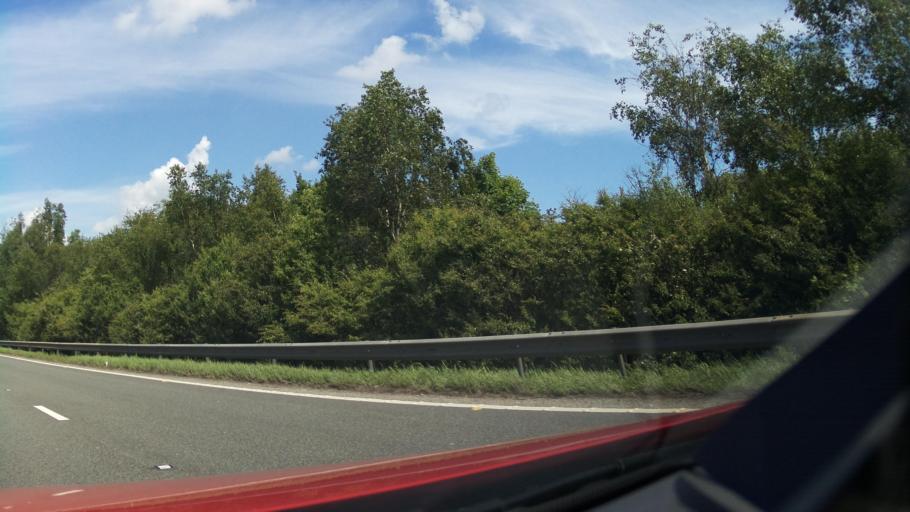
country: GB
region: England
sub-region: East Riding of Yorkshire
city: Rawcliffe
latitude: 53.6805
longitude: -0.9675
